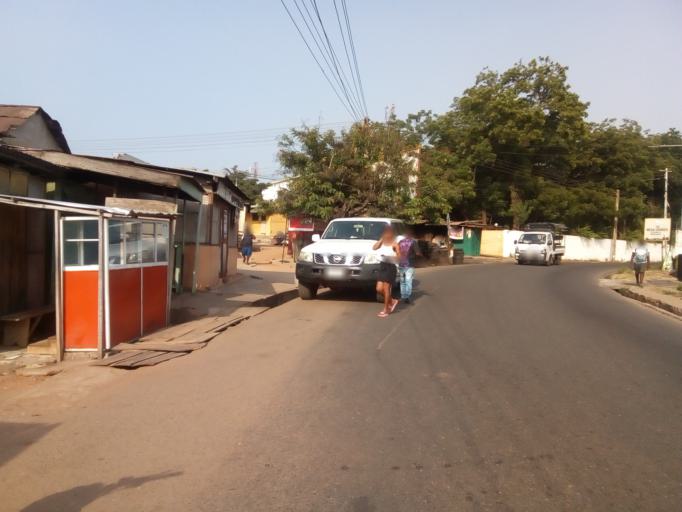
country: GH
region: Greater Accra
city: Accra
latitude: 5.5850
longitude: -0.2158
